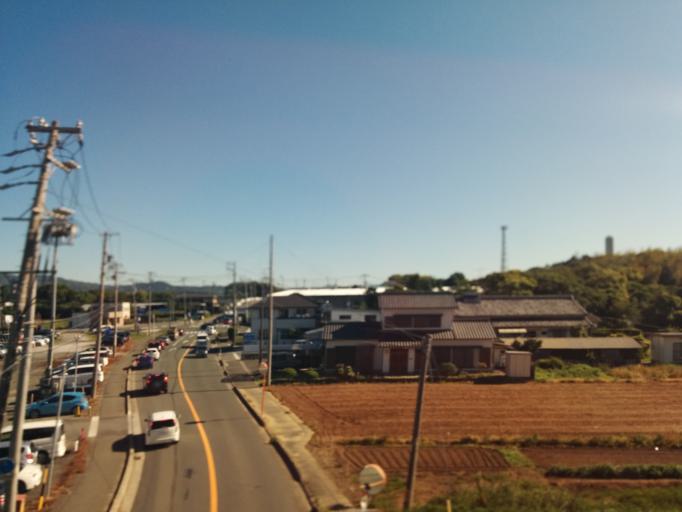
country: JP
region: Shizuoka
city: Kosai-shi
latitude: 34.7116
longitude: 137.4984
